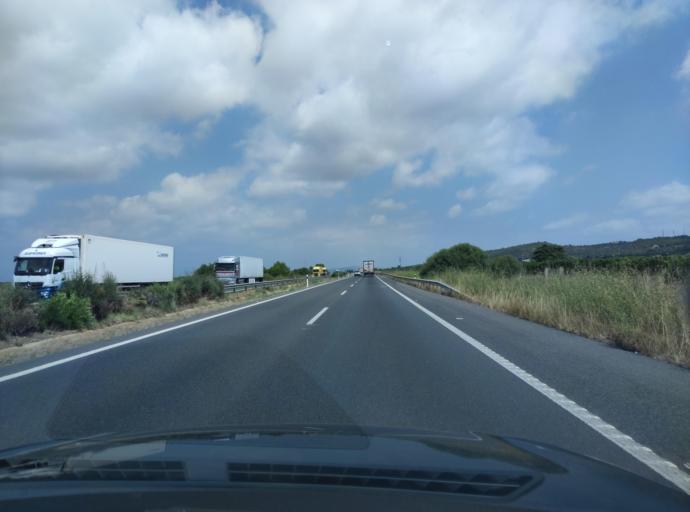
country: ES
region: Valencia
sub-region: Provincia de Castello
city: Vinaros
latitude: 40.4951
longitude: 0.4154
